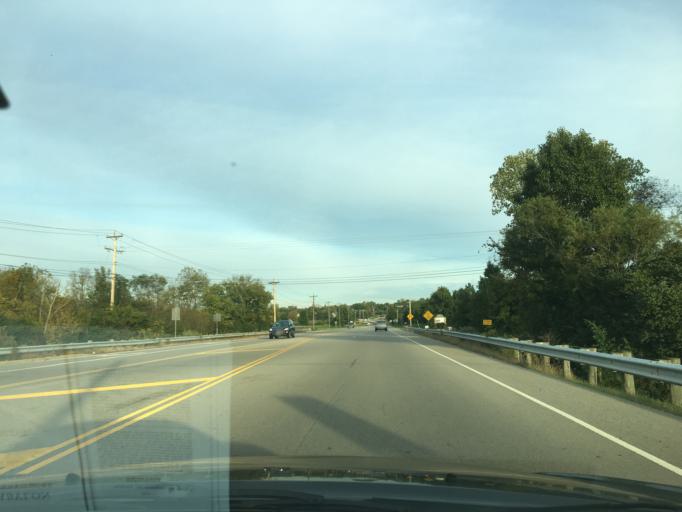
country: US
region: Ohio
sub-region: Butler County
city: Beckett Ridge
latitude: 39.3513
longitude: -84.4601
